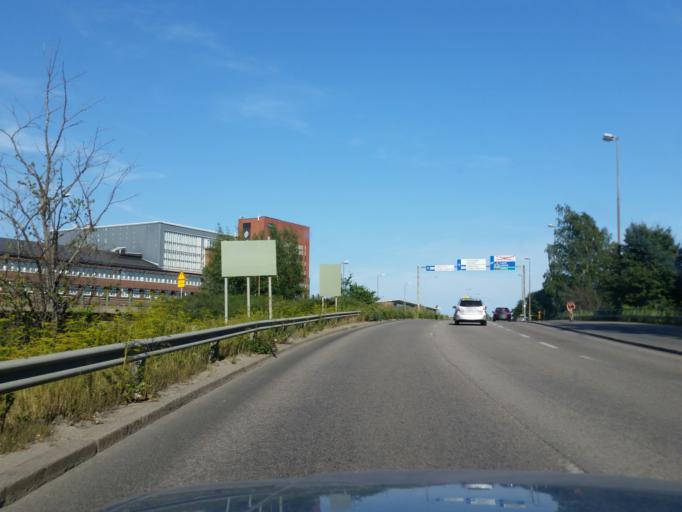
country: FI
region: Uusimaa
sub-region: Helsinki
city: Helsinki
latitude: 60.1876
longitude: 24.9717
